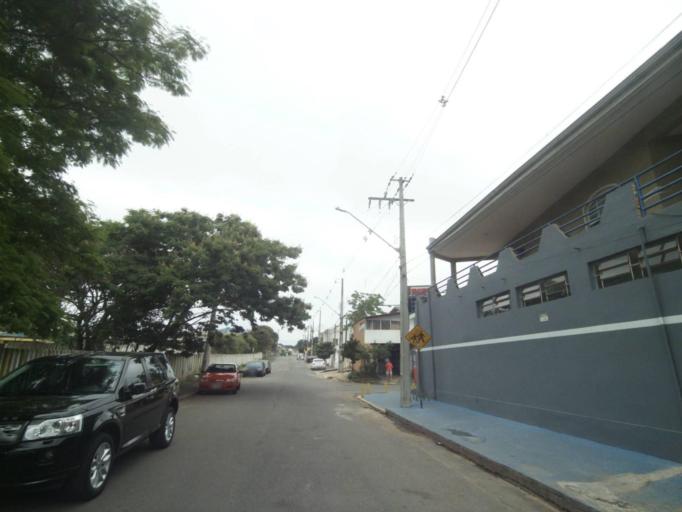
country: BR
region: Parana
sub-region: Curitiba
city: Curitiba
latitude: -25.4957
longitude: -49.3483
